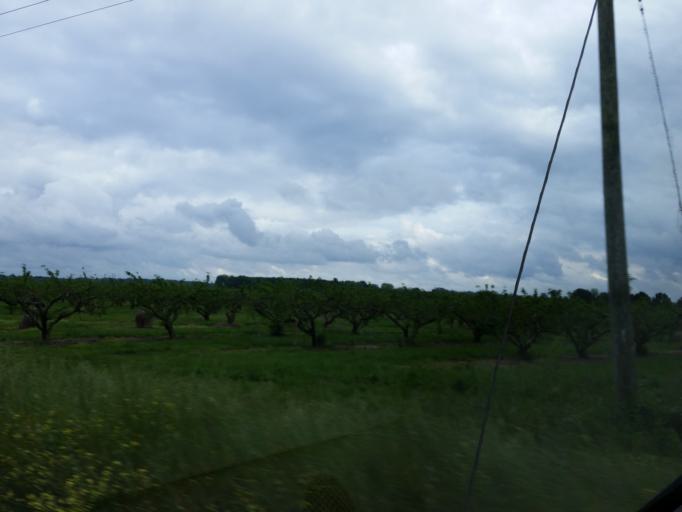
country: US
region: Georgia
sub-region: Peach County
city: Byron
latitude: 32.6641
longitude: -83.8230
